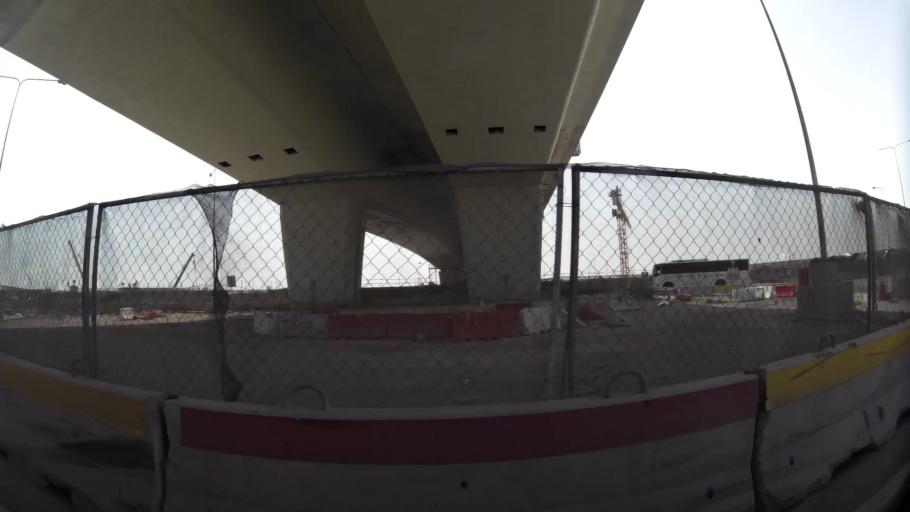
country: QA
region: Baladiyat ad Dawhah
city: Doha
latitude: 25.2265
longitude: 51.5089
